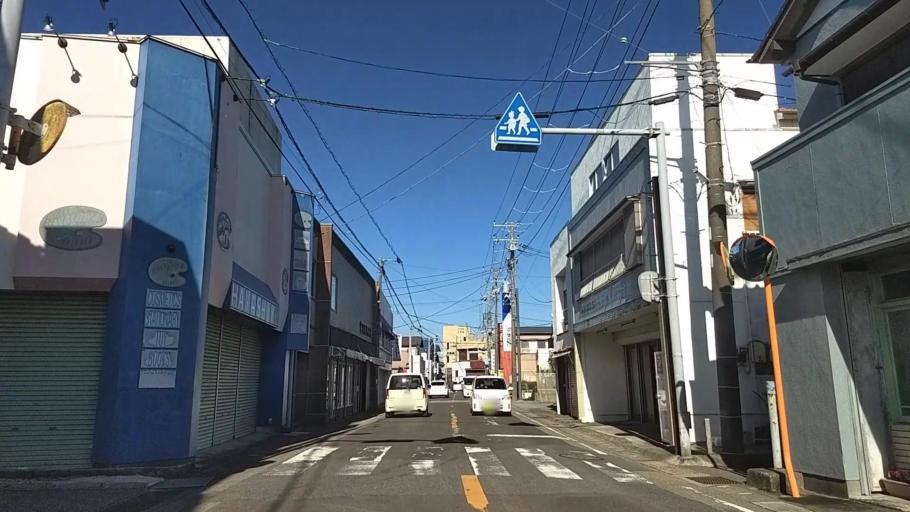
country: JP
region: Chiba
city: Tateyama
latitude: 34.9613
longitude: 139.9584
